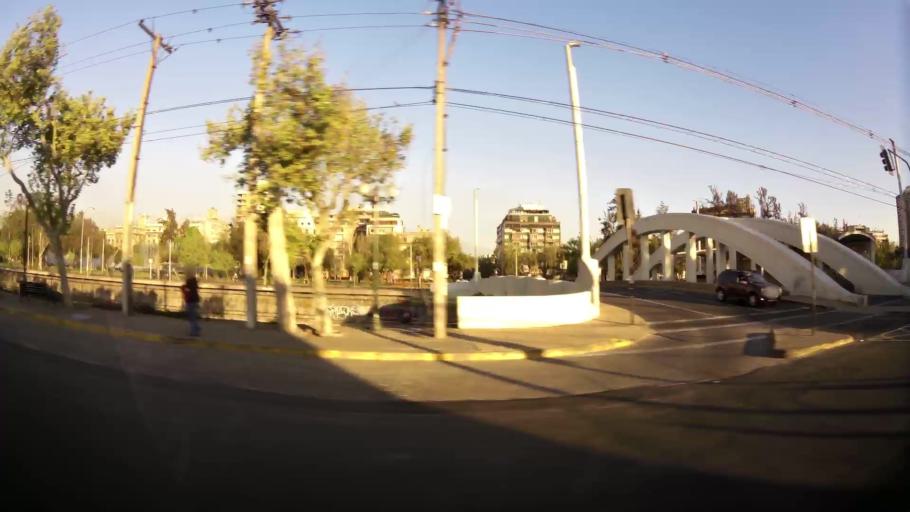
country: CL
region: Santiago Metropolitan
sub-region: Provincia de Santiago
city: Santiago
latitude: -33.4312
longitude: -70.6262
